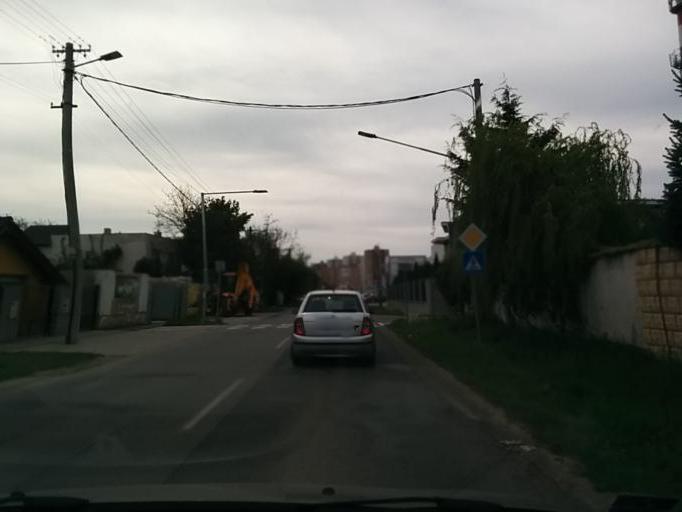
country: SK
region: Bratislavsky
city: Senec
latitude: 48.2239
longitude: 17.4084
